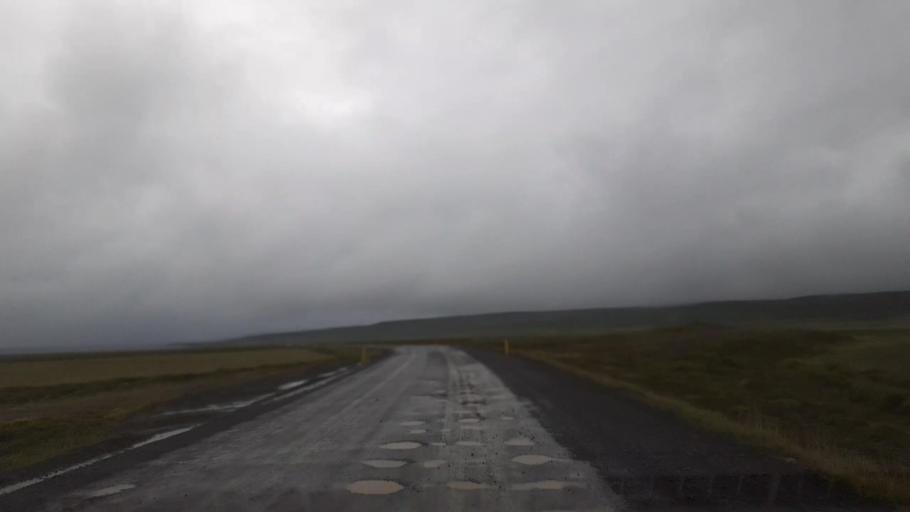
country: IS
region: East
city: Egilsstadir
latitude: 66.0335
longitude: -15.0562
